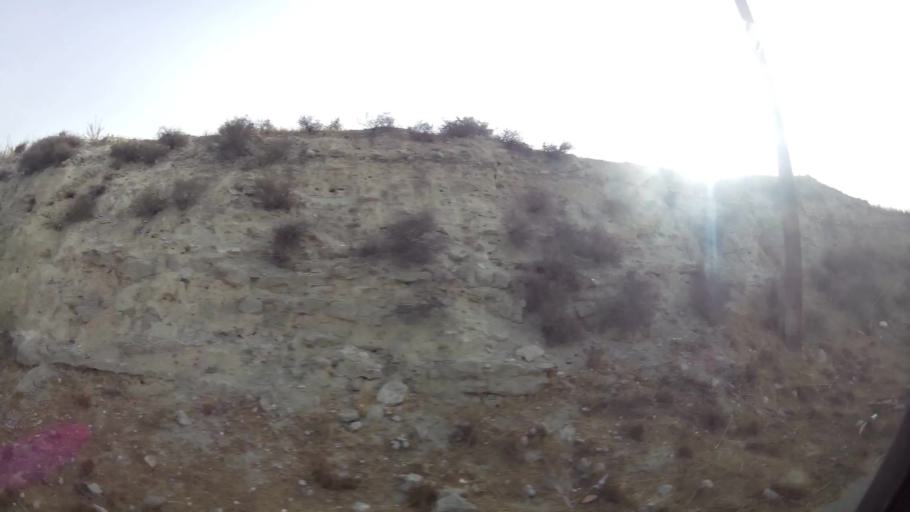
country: CY
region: Lefkosia
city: Dali
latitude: 35.0624
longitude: 33.3889
